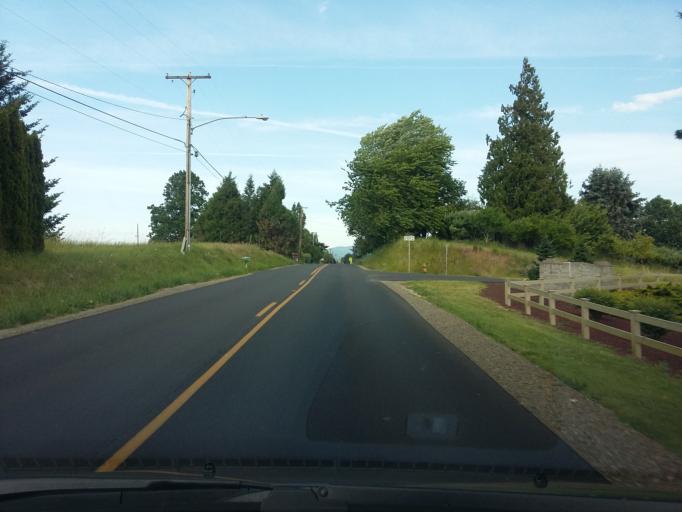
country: US
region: Washington
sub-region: Clark County
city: Barberton
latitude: 45.7186
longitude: -122.5777
